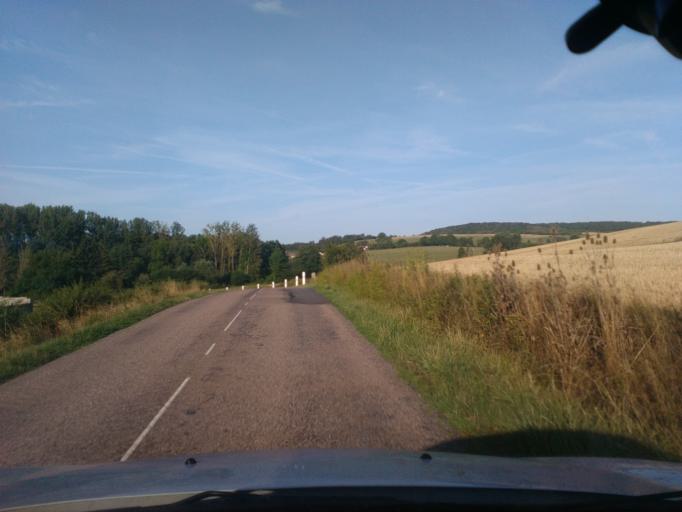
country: FR
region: Lorraine
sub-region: Departement des Vosges
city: Mirecourt
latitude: 48.2830
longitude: 6.0523
